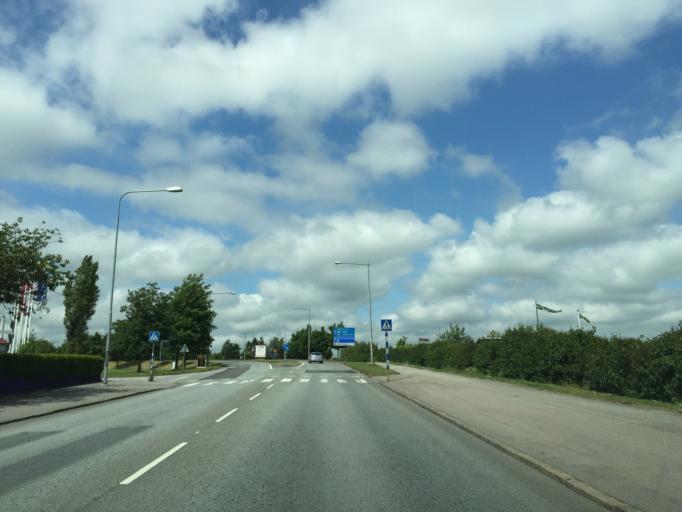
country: SE
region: Skane
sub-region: Ystads Kommun
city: Ystad
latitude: 55.4416
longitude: 13.8354
